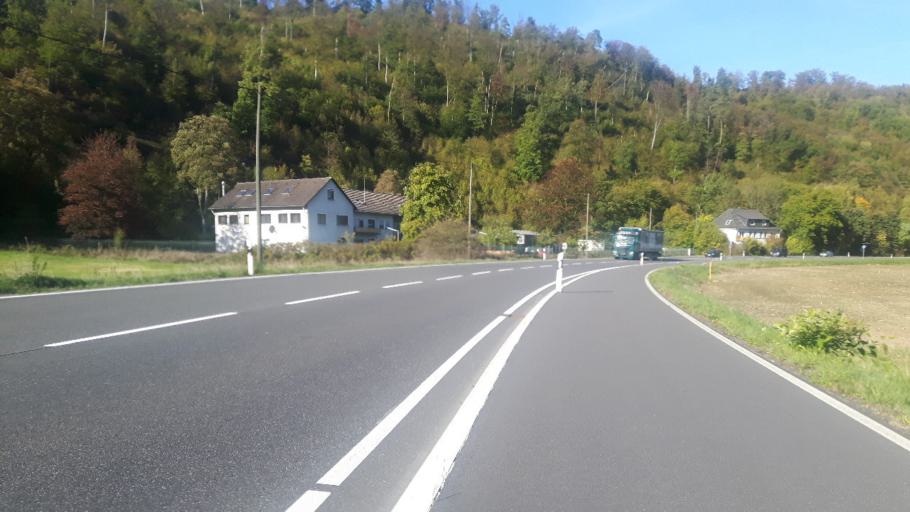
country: DE
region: Rheinland-Pfalz
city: Mittelhof
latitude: 50.8022
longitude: 7.7849
